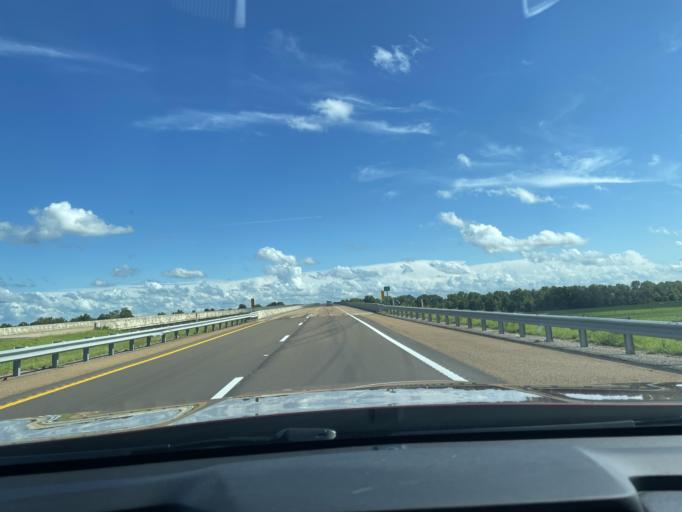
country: US
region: Mississippi
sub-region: Yazoo County
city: Yazoo City
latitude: 32.9334
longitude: -90.4130
